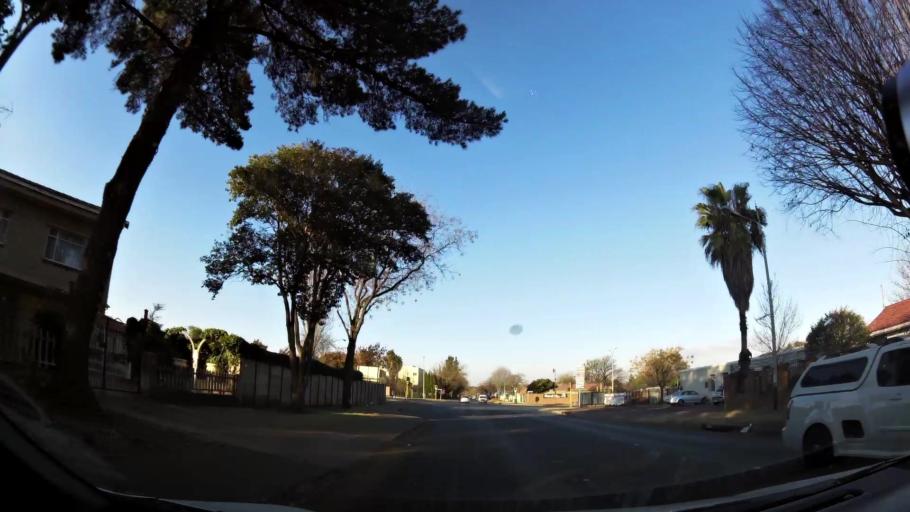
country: ZA
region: Gauteng
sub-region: Ekurhuleni Metropolitan Municipality
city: Germiston
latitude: -26.2738
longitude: 28.1183
